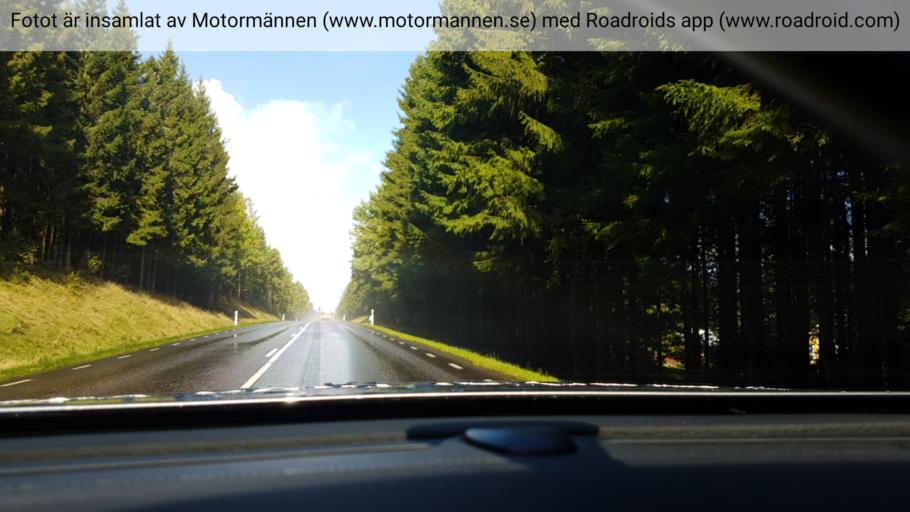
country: SE
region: Vaestra Goetaland
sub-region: Alingsas Kommun
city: Sollebrunn
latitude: 58.0262
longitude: 12.4609
